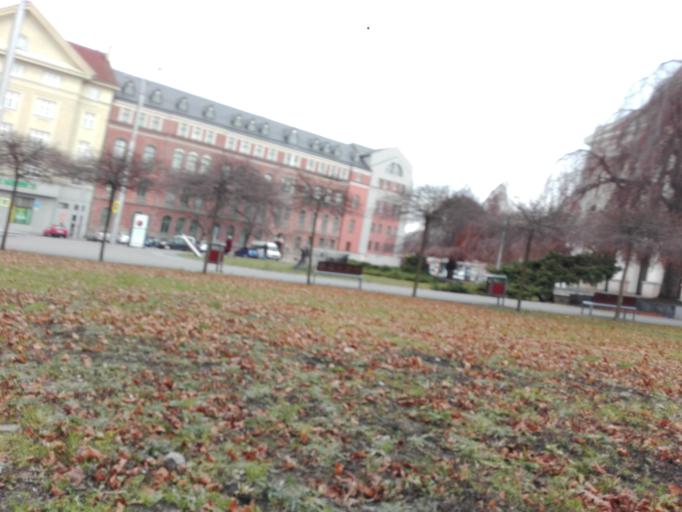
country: CZ
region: Moravskoslezsky
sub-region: Okres Ostrava-Mesto
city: Ostrava
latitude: 49.8323
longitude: 18.2902
